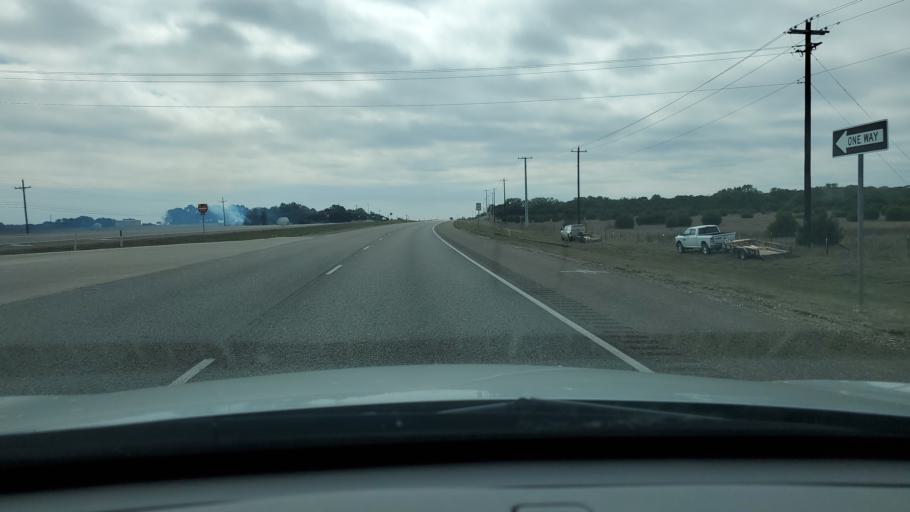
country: US
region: Texas
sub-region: Williamson County
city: Florence
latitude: 30.8018
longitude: -97.7691
